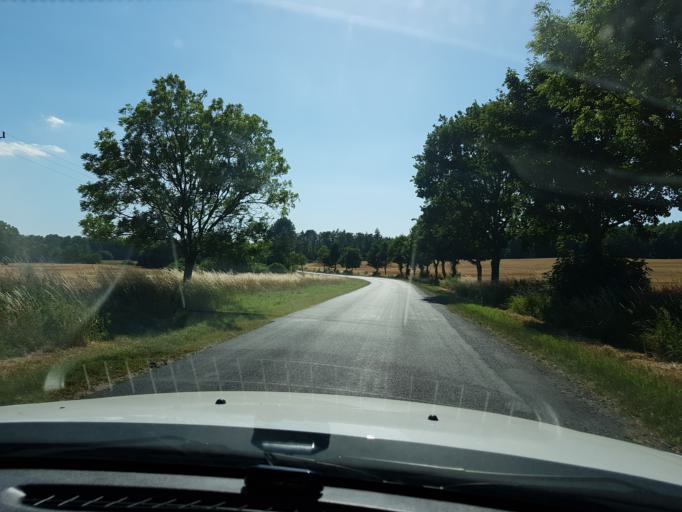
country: PL
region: West Pomeranian Voivodeship
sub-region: Powiat bialogardzki
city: Karlino
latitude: 53.9539
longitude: 15.8716
